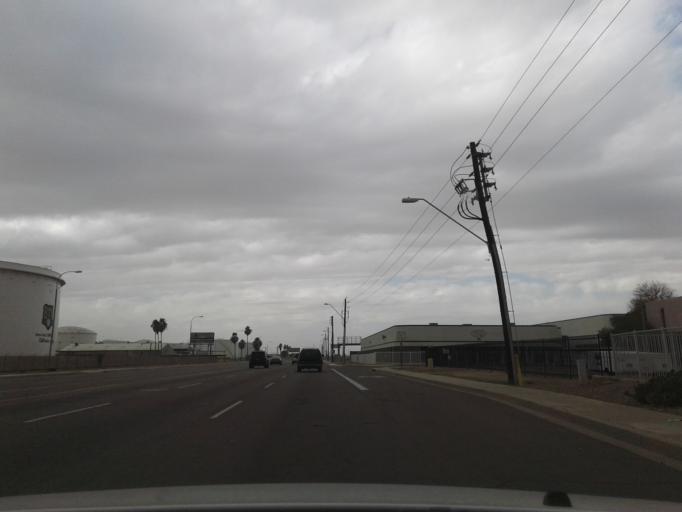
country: US
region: Arizona
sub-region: Maricopa County
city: Tolleson
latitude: 33.4513
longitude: -112.1712
